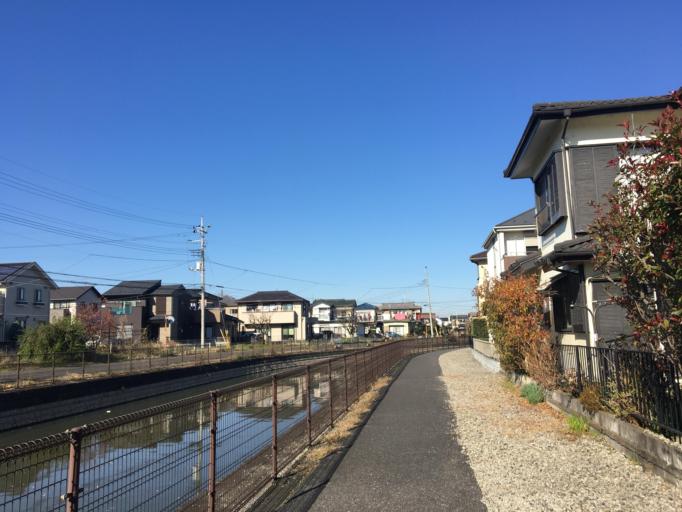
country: JP
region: Saitama
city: Satte
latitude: 36.0700
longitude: 139.7087
